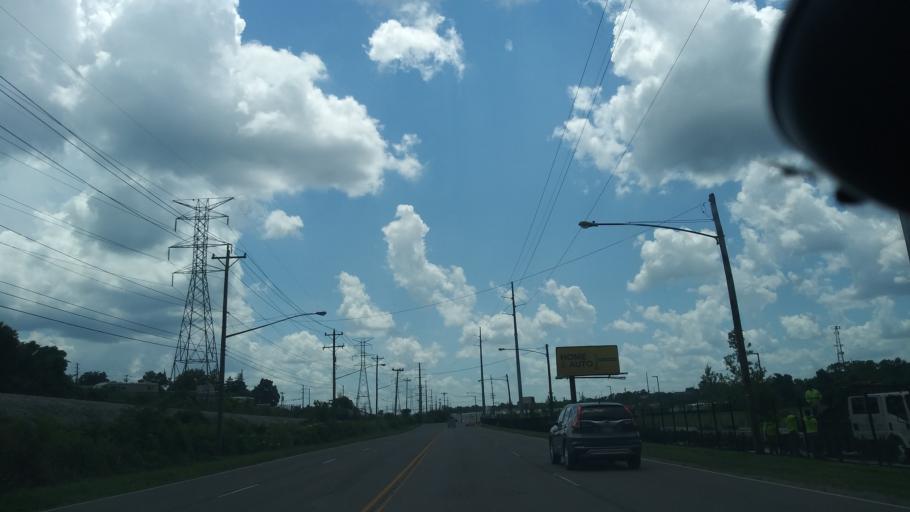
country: US
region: Tennessee
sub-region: Davidson County
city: Nashville
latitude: 36.1276
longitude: -86.7624
